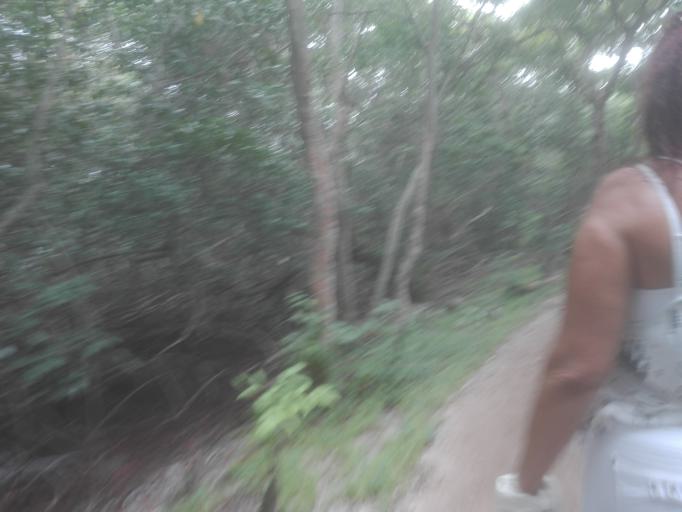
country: CO
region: Bolivar
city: Turbana
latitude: 10.1748
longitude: -75.7423
